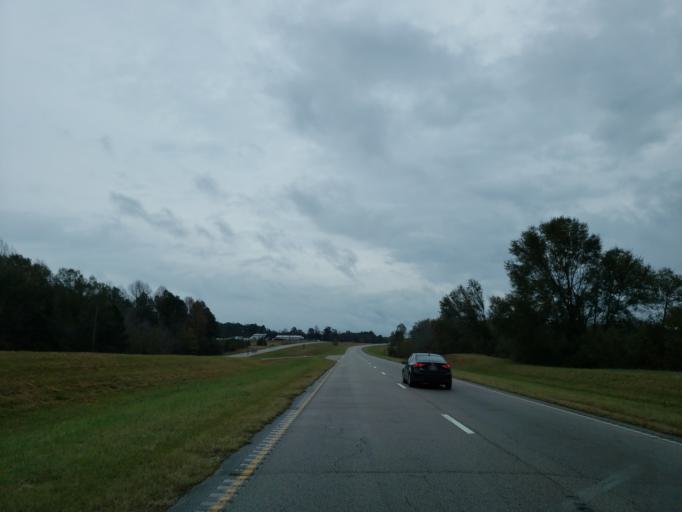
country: US
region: Mississippi
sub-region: Jones County
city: Sharon
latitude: 31.7034
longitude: -88.9153
